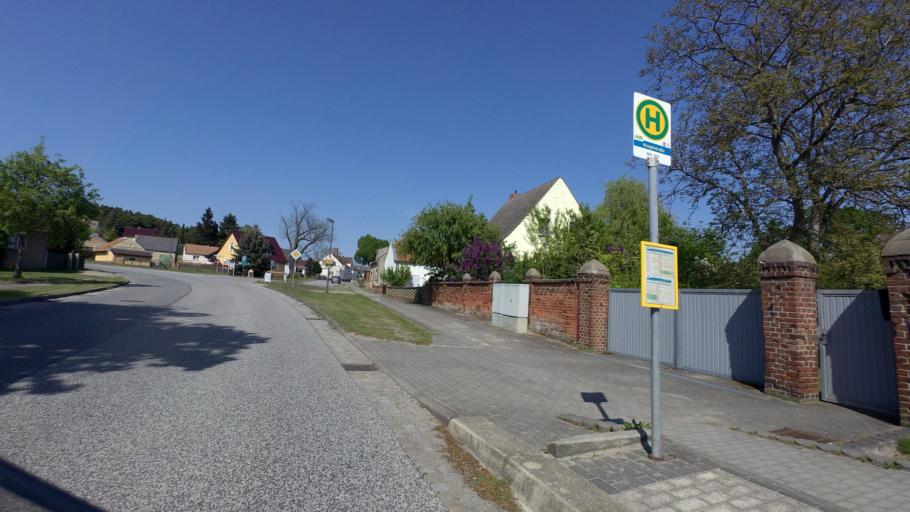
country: DE
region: Brandenburg
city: Neu Zauche
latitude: 52.0377
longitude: 14.0380
